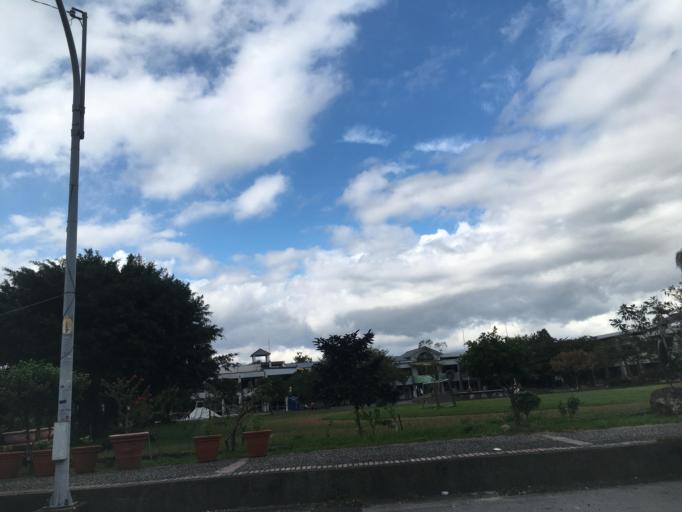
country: TW
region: Taiwan
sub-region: Yilan
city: Yilan
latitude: 24.6920
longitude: 121.7281
